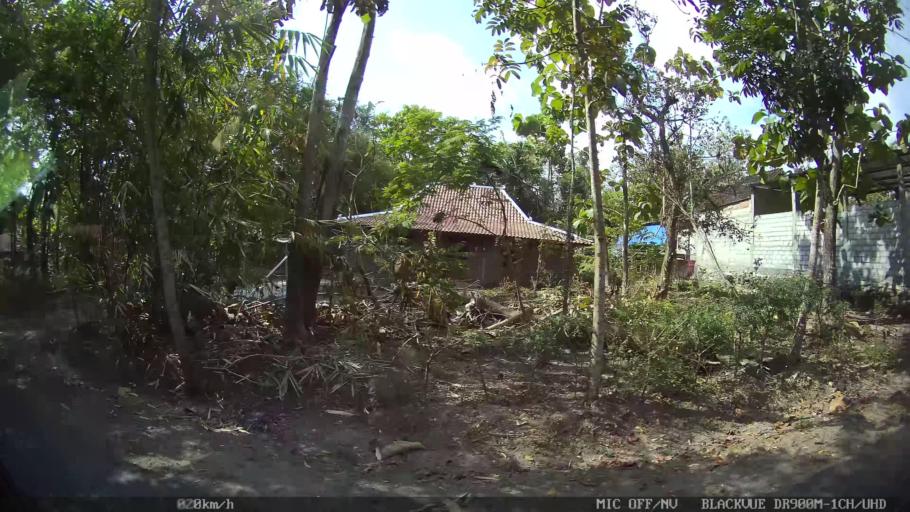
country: ID
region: Daerah Istimewa Yogyakarta
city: Kasihan
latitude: -7.8502
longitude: 110.2995
